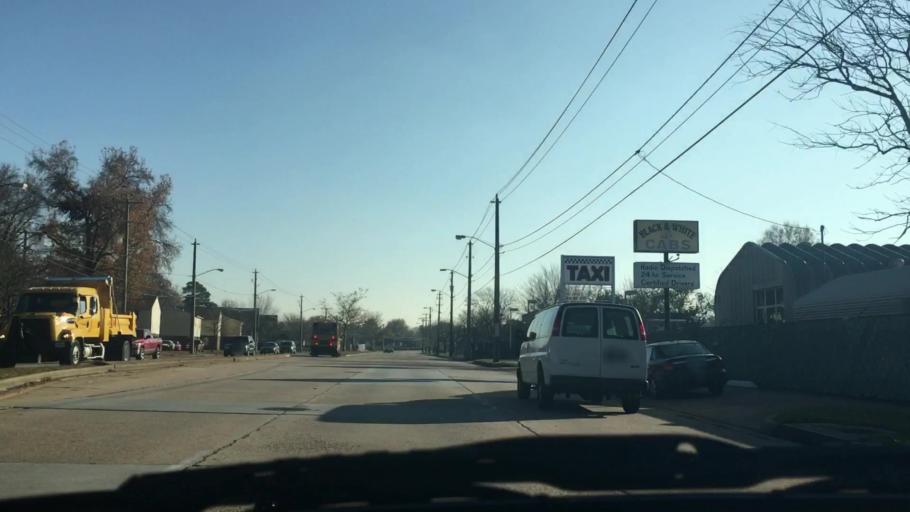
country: US
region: Virginia
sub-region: City of Norfolk
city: Norfolk
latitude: 36.8944
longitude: -76.2383
